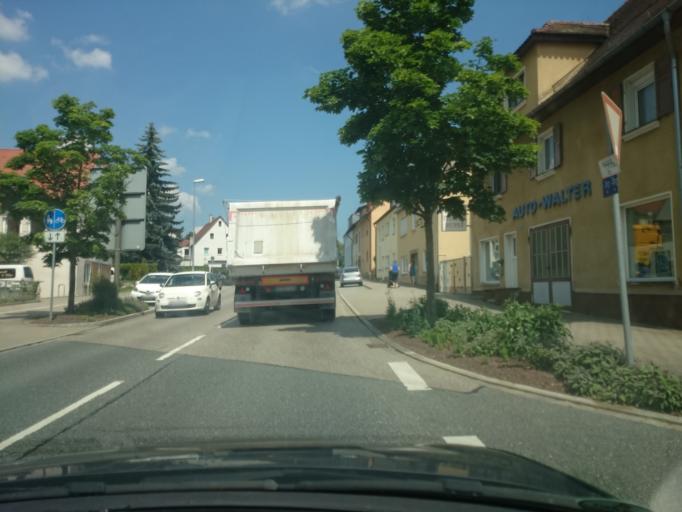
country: DE
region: Bavaria
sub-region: Regierungsbezirk Mittelfranken
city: Hilpoltstein
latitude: 49.1862
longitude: 11.1916
